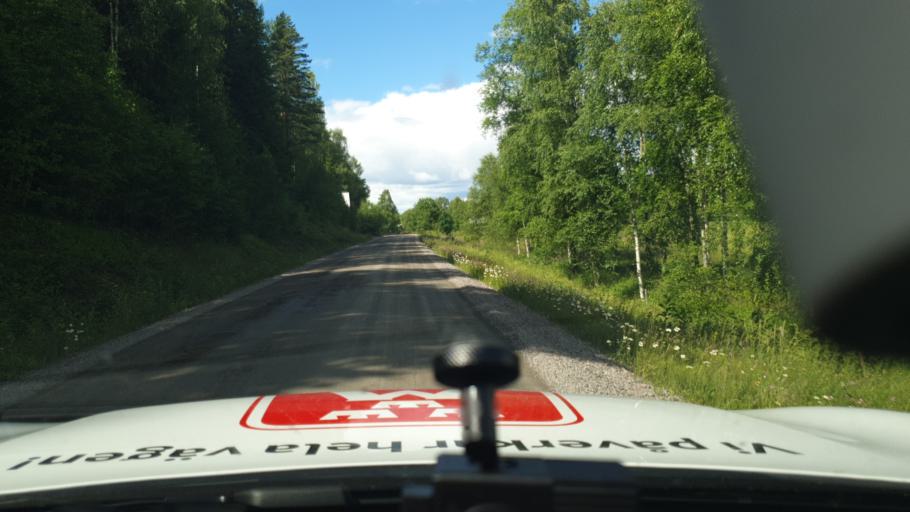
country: SE
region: Vaermland
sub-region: Hagfors Kommun
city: Ekshaerad
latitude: 60.4249
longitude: 13.2434
